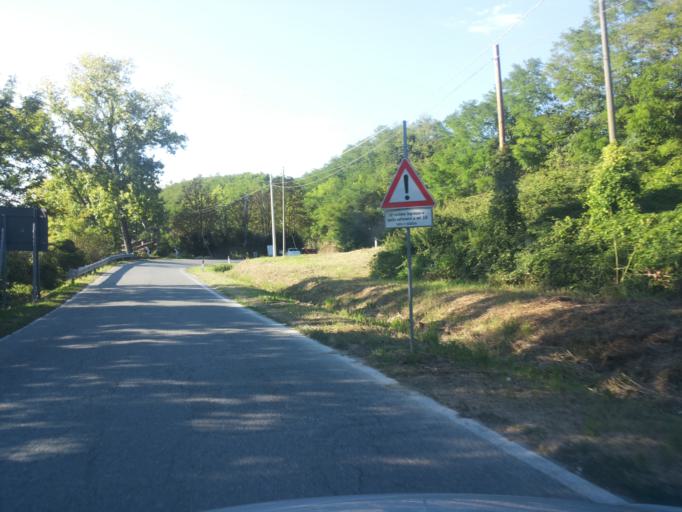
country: IT
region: Piedmont
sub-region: Provincia di Torino
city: Vestigne
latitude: 45.3986
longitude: 7.9427
